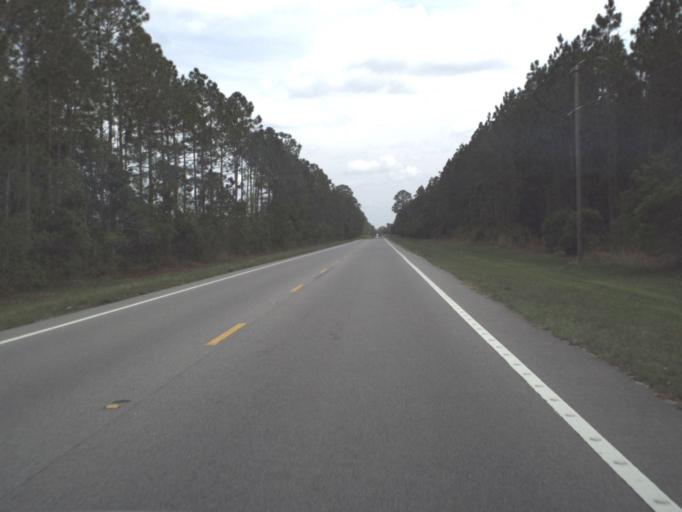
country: US
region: Florida
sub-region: Putnam County
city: Crescent City
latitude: 29.5333
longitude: -81.5172
